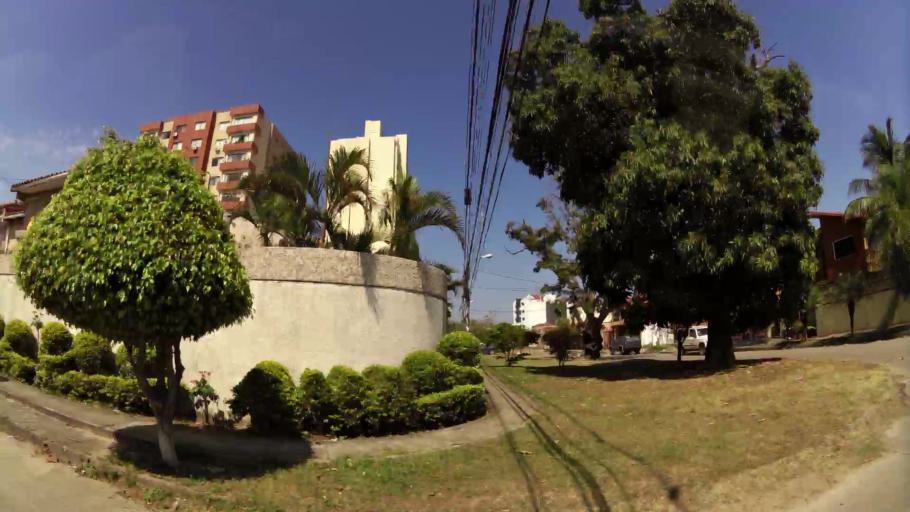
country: BO
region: Santa Cruz
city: Santa Cruz de la Sierra
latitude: -17.7437
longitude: -63.1690
